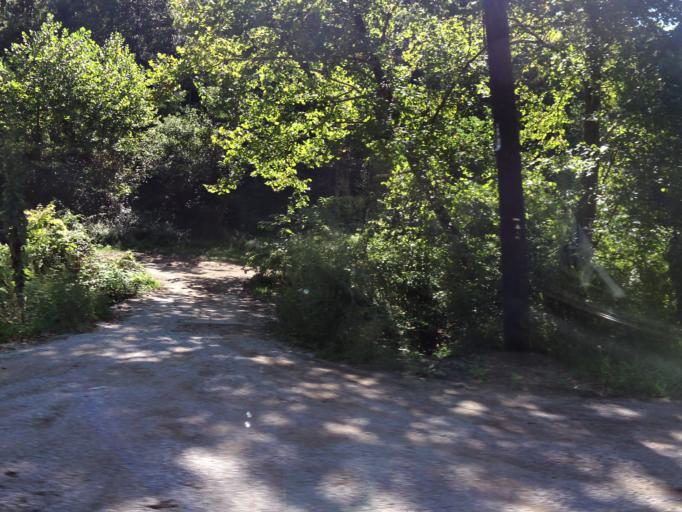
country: US
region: Kentucky
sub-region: Clay County
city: Manchester
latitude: 37.1182
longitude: -83.6394
